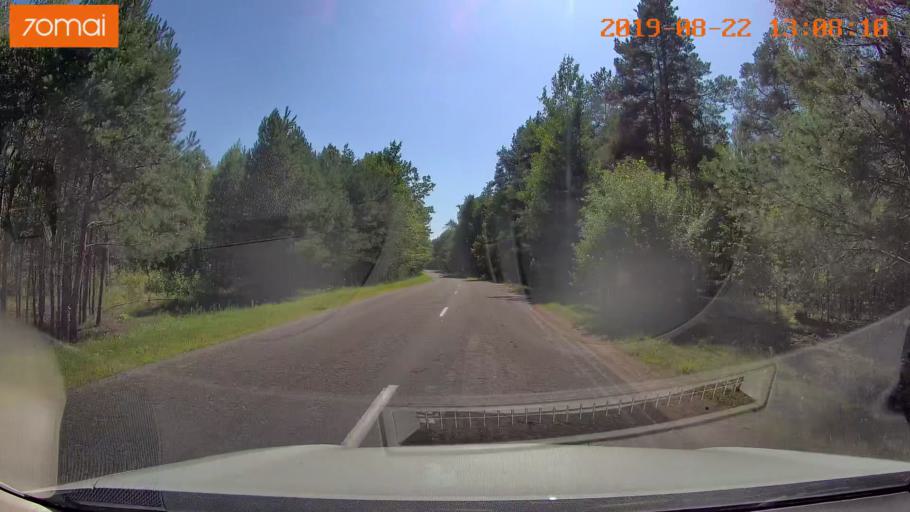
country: BY
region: Minsk
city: Prawdzinski
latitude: 53.3276
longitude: 27.8428
